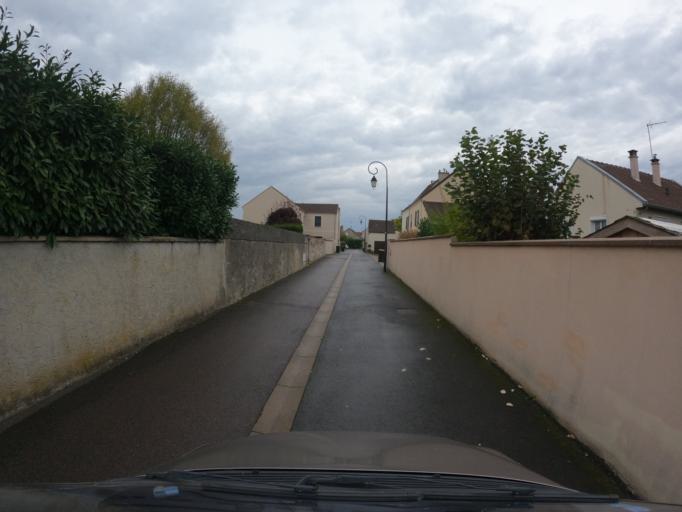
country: FR
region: Ile-de-France
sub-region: Departement de Seine-et-Marne
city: Villeneuve-le-Comte
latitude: 48.8148
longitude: 2.8265
